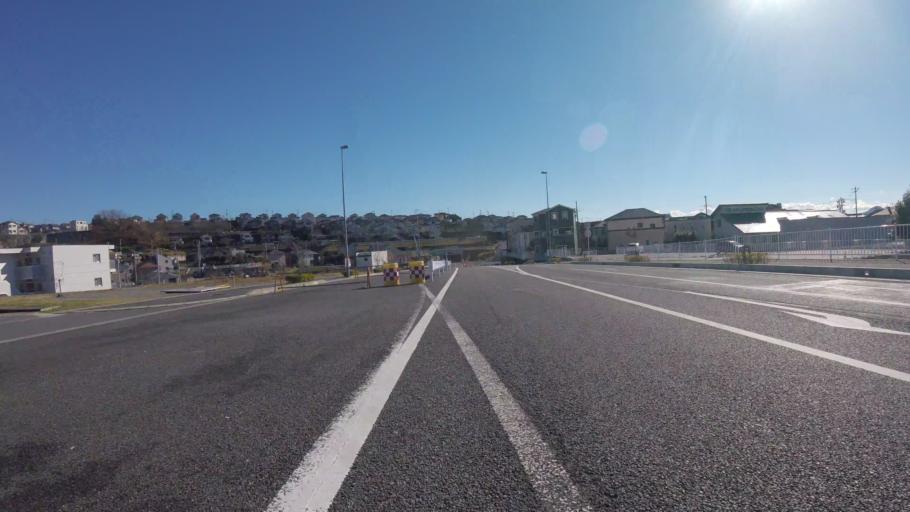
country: JP
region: Shizuoka
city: Mishima
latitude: 35.1345
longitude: 138.9206
